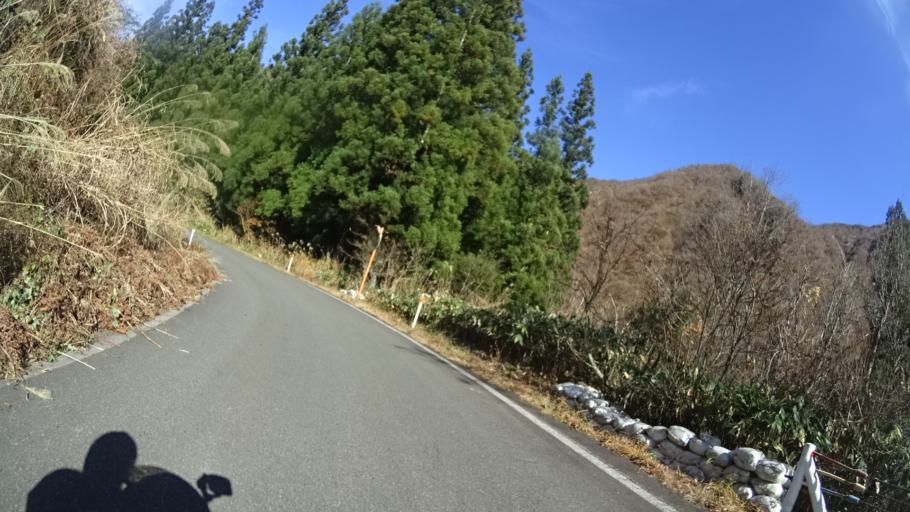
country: JP
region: Niigata
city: Muikamachi
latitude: 37.1778
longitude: 139.0869
